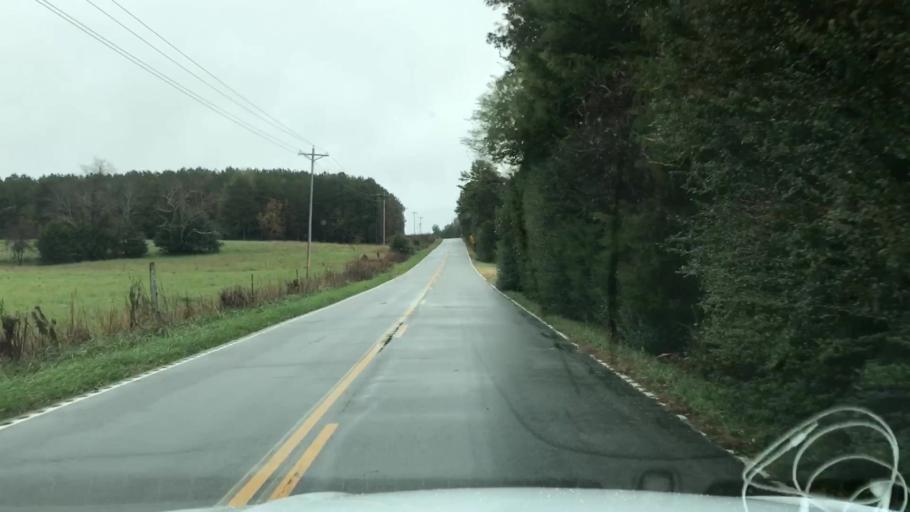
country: US
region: South Carolina
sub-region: Spartanburg County
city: Woodruff
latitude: 34.7614
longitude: -81.9171
